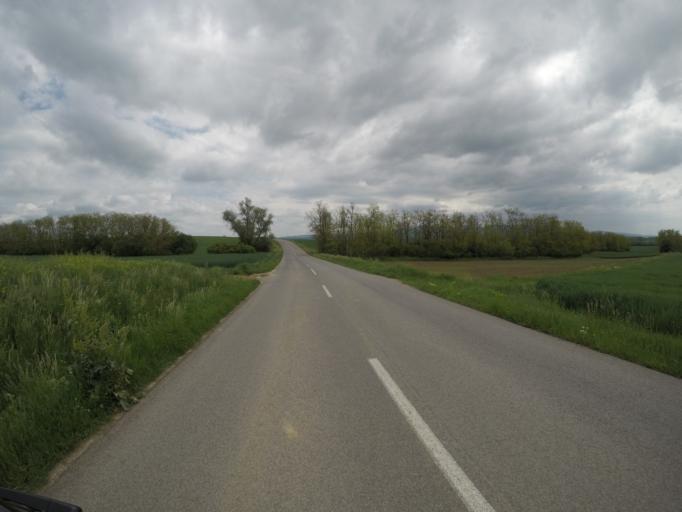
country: SK
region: Banskobystricky
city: Dudince
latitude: 48.0733
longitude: 18.8312
